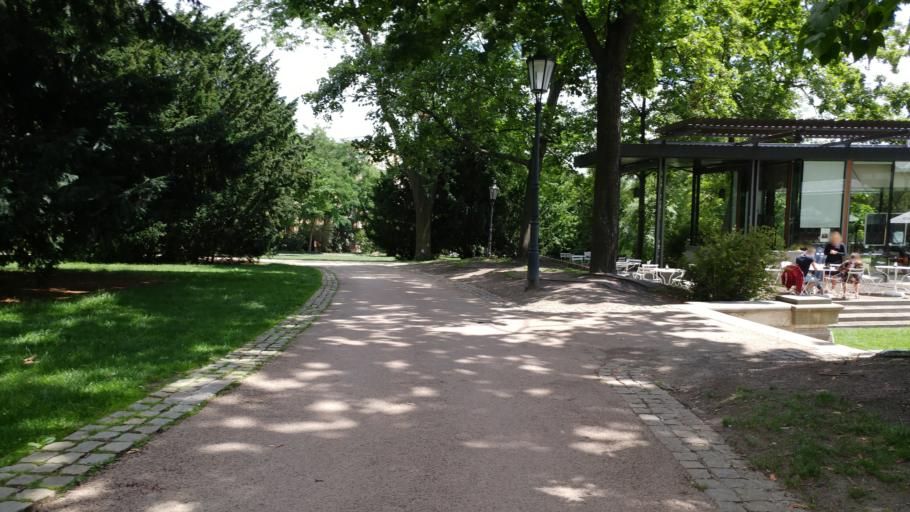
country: CZ
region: Praha
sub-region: Praha 8
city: Karlin
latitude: 50.0700
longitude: 14.4453
